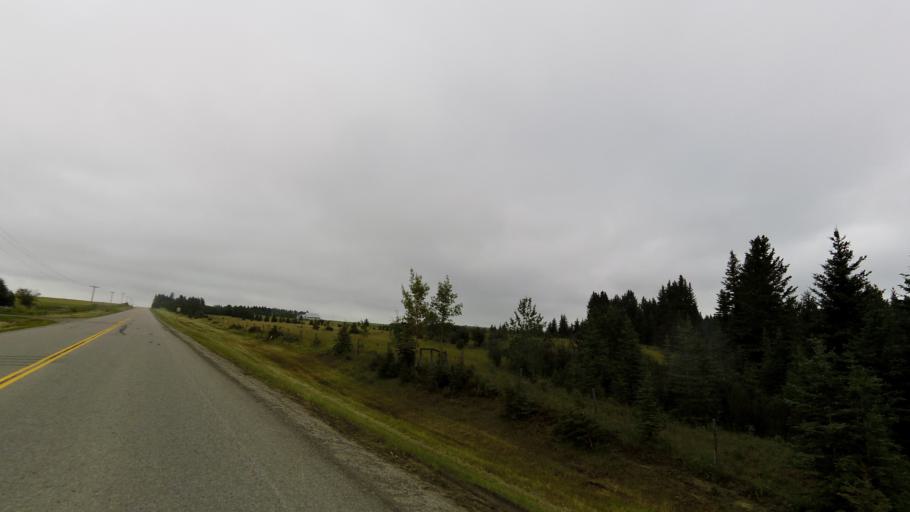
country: CA
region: Alberta
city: Rocky Mountain House
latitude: 52.4067
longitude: -114.9348
